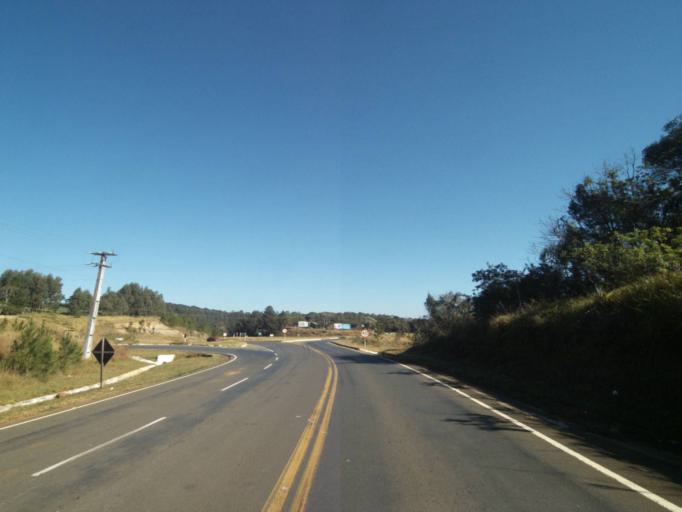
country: BR
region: Parana
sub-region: Tibagi
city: Tibagi
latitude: -24.5007
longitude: -50.4432
